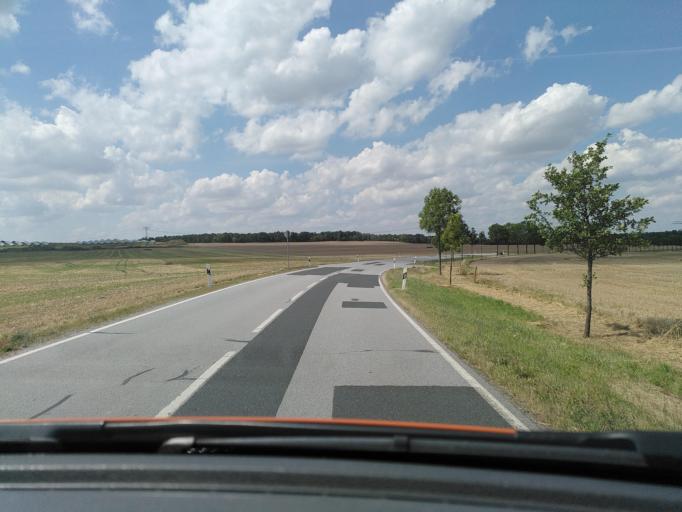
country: DE
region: Saxony
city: Kubschutz
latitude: 51.1829
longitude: 14.4839
